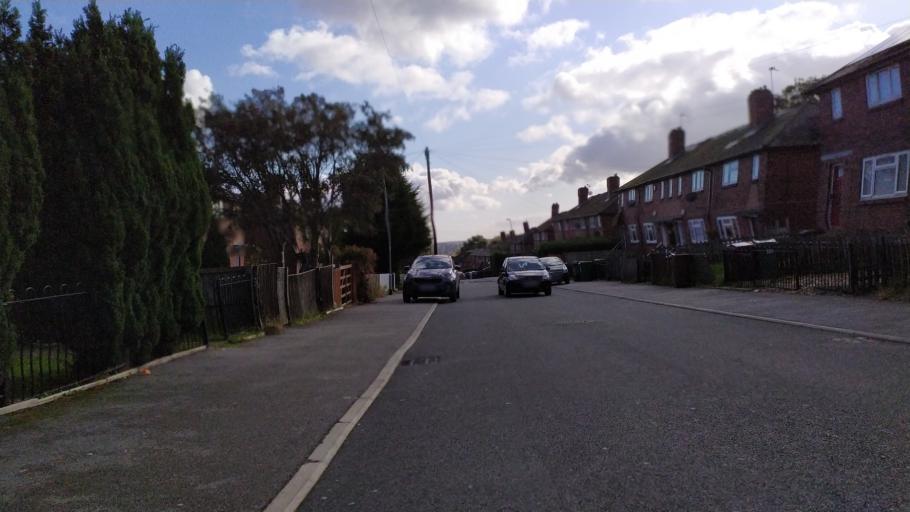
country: GB
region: England
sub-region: City and Borough of Leeds
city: Chapel Allerton
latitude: 53.8190
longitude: -1.5425
